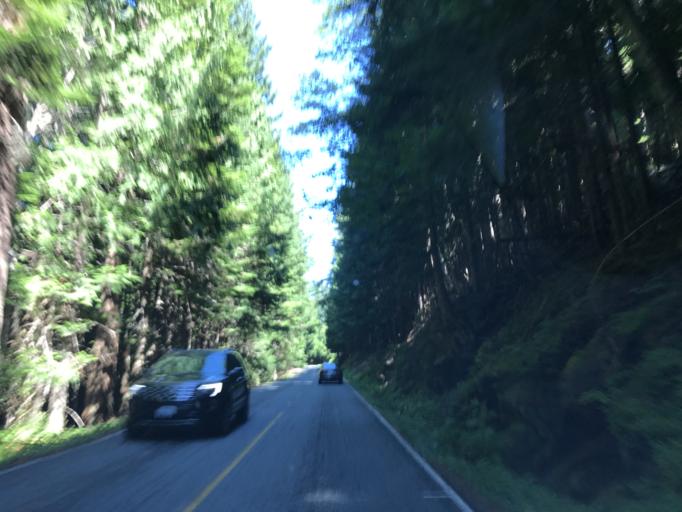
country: US
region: Washington
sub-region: King County
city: Enumclaw
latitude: 46.9122
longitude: -121.5374
